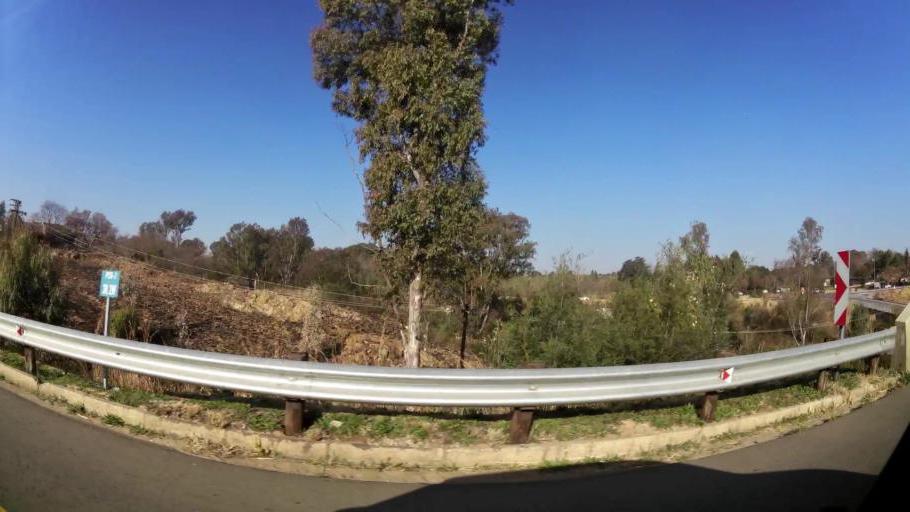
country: ZA
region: Gauteng
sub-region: West Rand District Municipality
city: Muldersdriseloop
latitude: -26.0370
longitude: 27.8457
